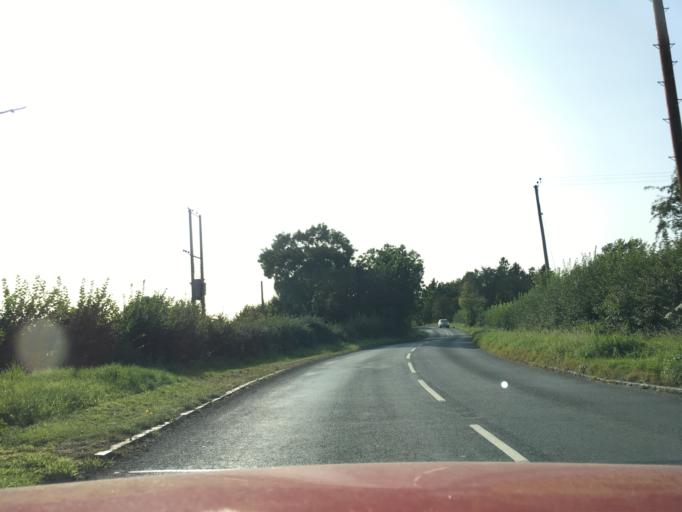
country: GB
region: England
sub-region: Gloucestershire
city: Tewkesbury
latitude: 51.9442
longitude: -2.2024
